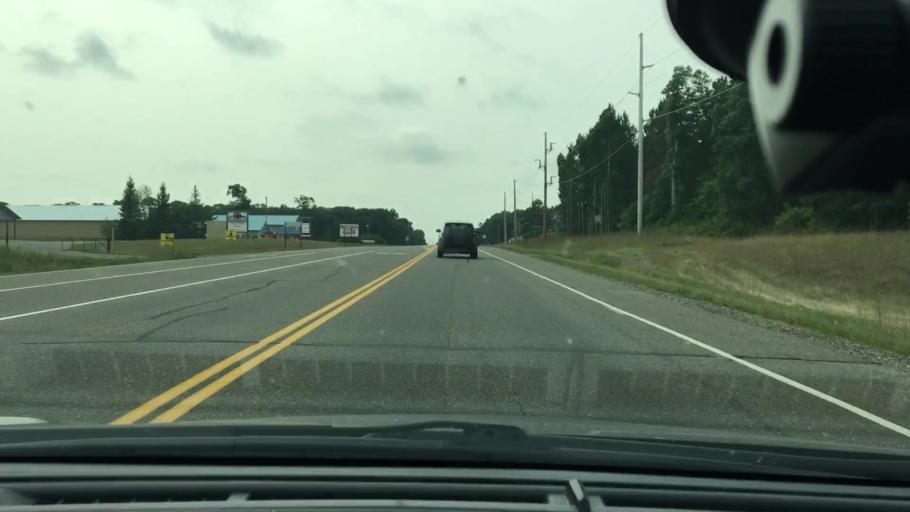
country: US
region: Minnesota
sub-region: Crow Wing County
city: Cross Lake
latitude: 46.6166
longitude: -94.1319
